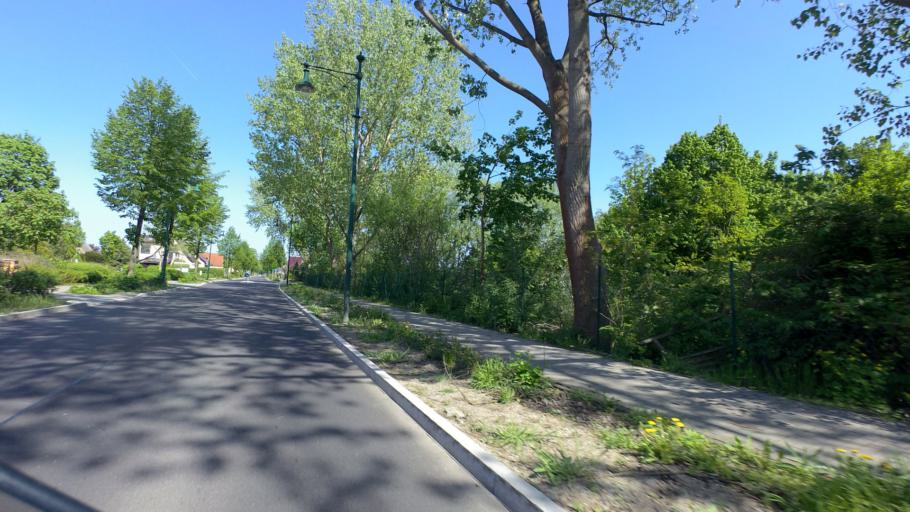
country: DE
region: Brandenburg
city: Beeskow
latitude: 52.1694
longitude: 14.2625
